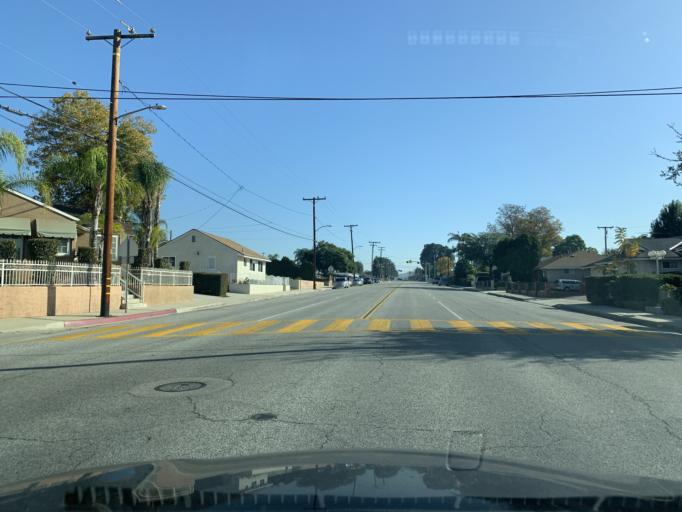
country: US
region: California
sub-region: Los Angeles County
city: Covina
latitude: 34.0825
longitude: -117.8771
